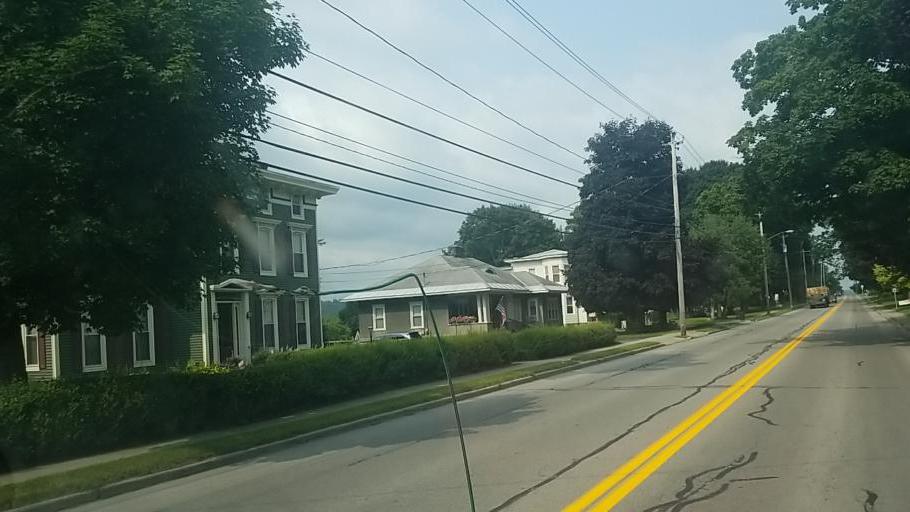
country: US
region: New York
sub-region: Montgomery County
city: Canajoharie
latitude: 42.9117
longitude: -74.5770
